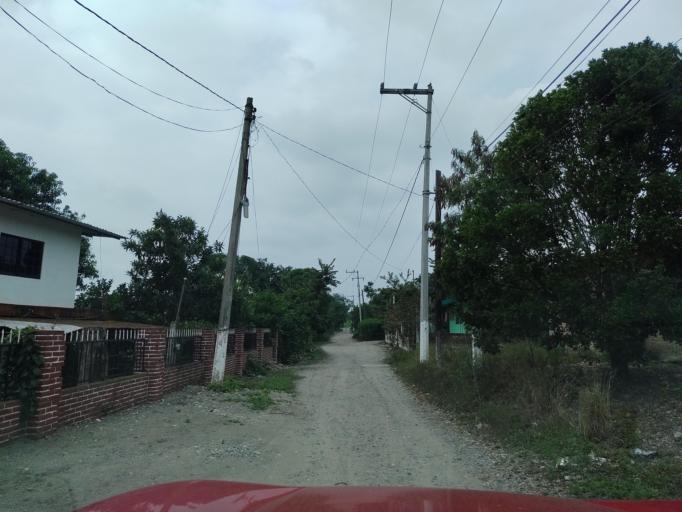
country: MX
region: Veracruz
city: Agua Dulce
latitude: 20.3415
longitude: -97.2924
